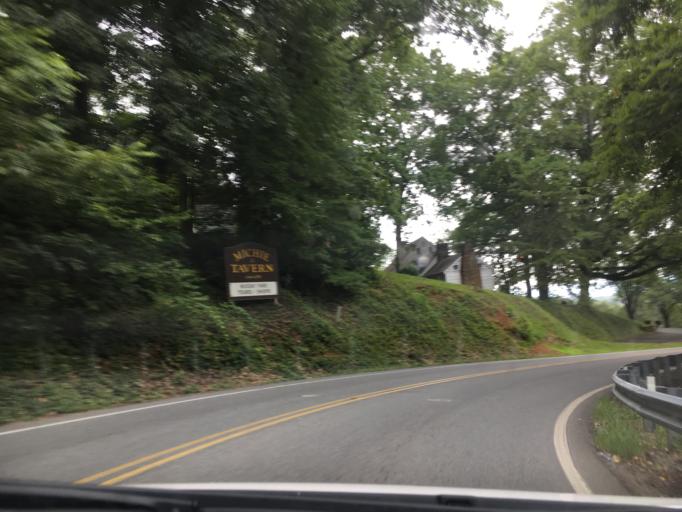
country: US
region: Virginia
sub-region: City of Charlottesville
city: Charlottesville
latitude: 38.0085
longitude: -78.4626
